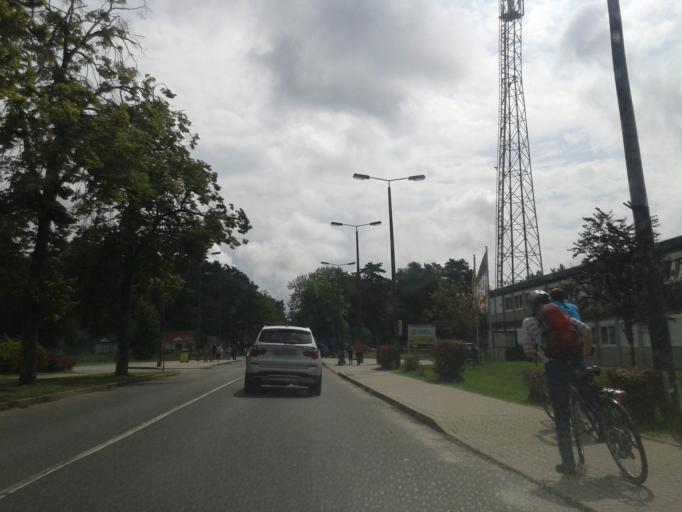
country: PL
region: West Pomeranian Voivodeship
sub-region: Swinoujscie
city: Swinoujscie
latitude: 53.9227
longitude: 14.2161
